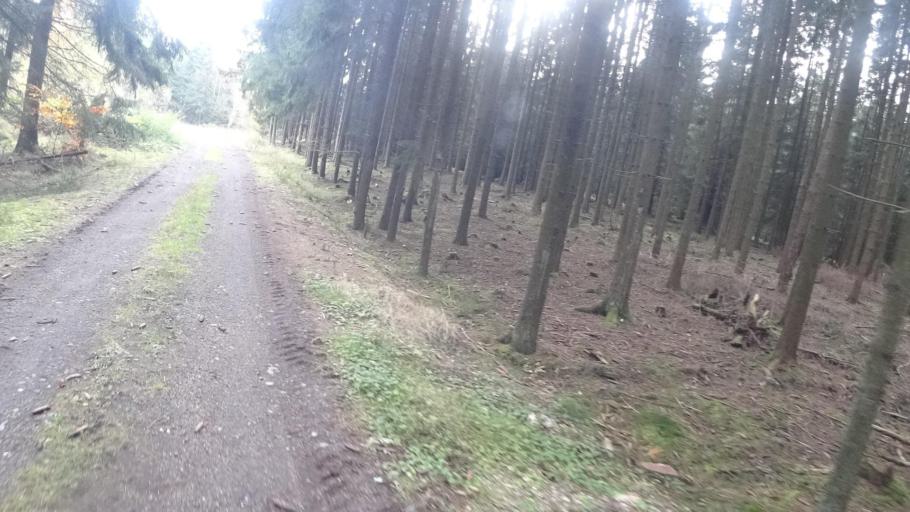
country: DE
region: Rheinland-Pfalz
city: Hausbay
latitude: 50.0995
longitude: 7.5378
